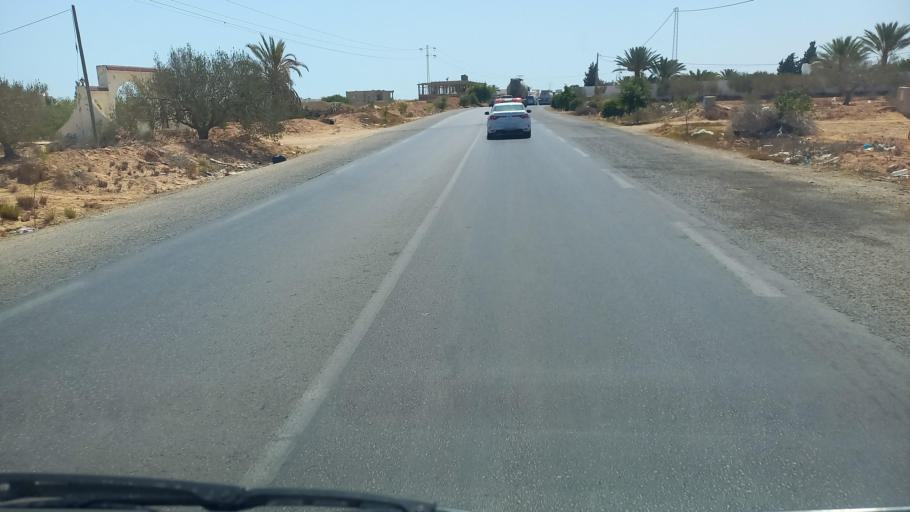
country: TN
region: Madanin
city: Houmt Souk
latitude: 33.8110
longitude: 10.8783
